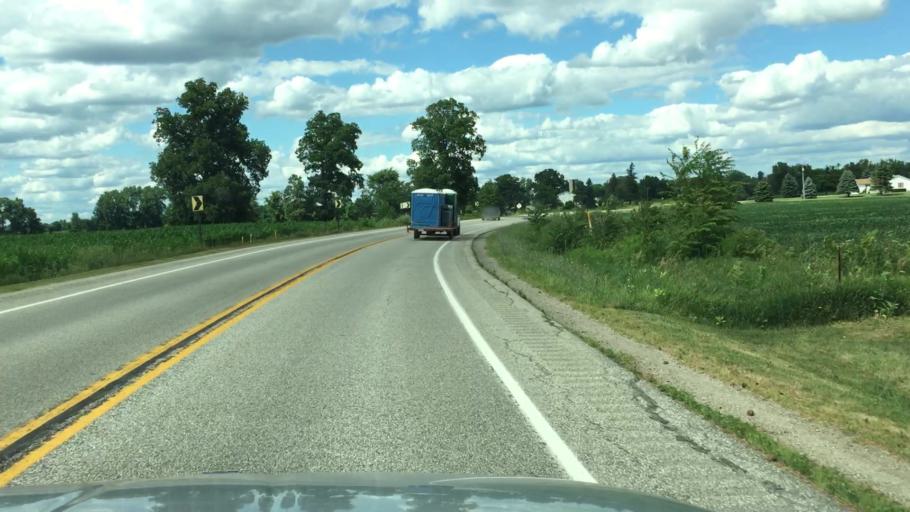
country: US
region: Michigan
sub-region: Saint Clair County
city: Capac
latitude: 42.9436
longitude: -82.9459
